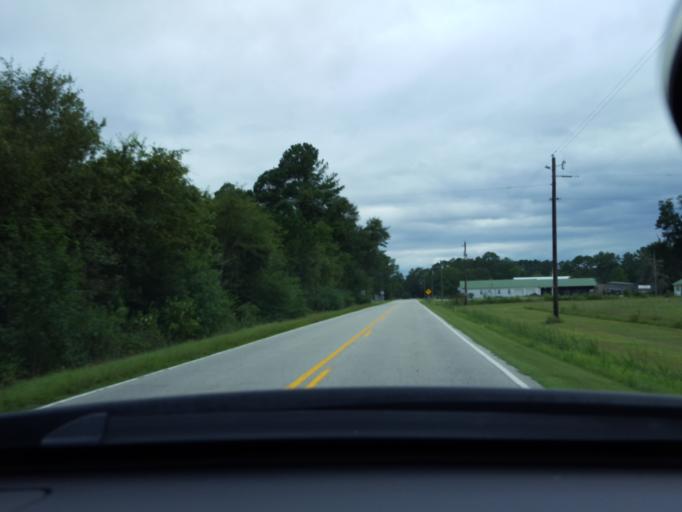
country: US
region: North Carolina
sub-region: Sampson County
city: Roseboro
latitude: 34.7837
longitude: -78.3848
